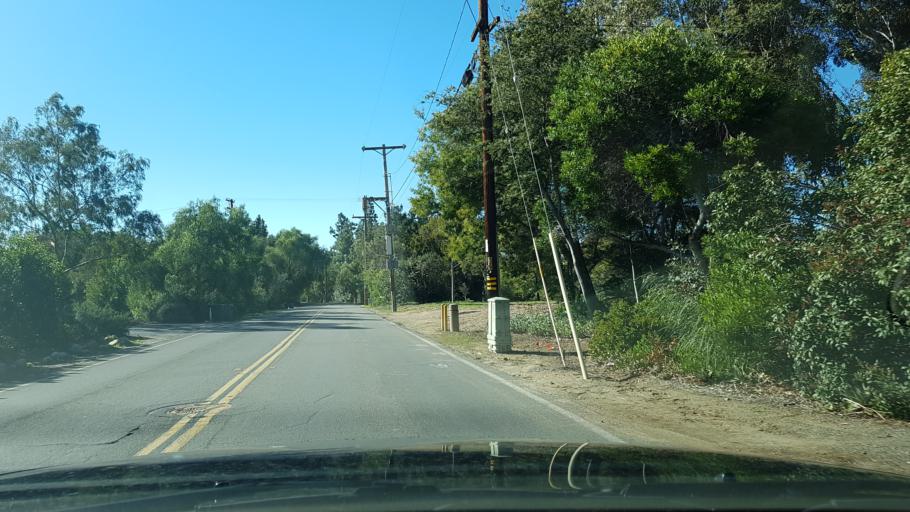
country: US
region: California
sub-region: San Diego County
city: Rancho Santa Fe
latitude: 33.0372
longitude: -117.2138
